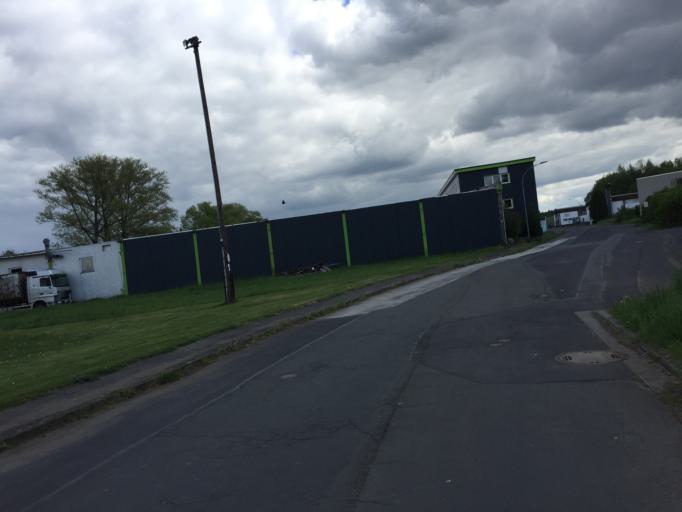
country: DE
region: Hesse
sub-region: Regierungsbezirk Giessen
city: Grunberg
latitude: 50.5729
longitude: 8.9316
